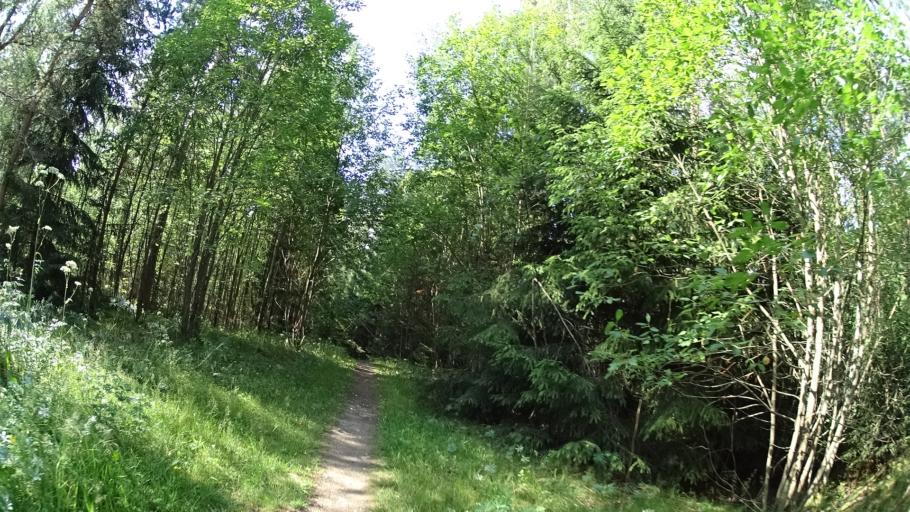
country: FI
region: Uusimaa
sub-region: Helsinki
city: Teekkarikylae
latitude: 60.2900
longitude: 24.9026
